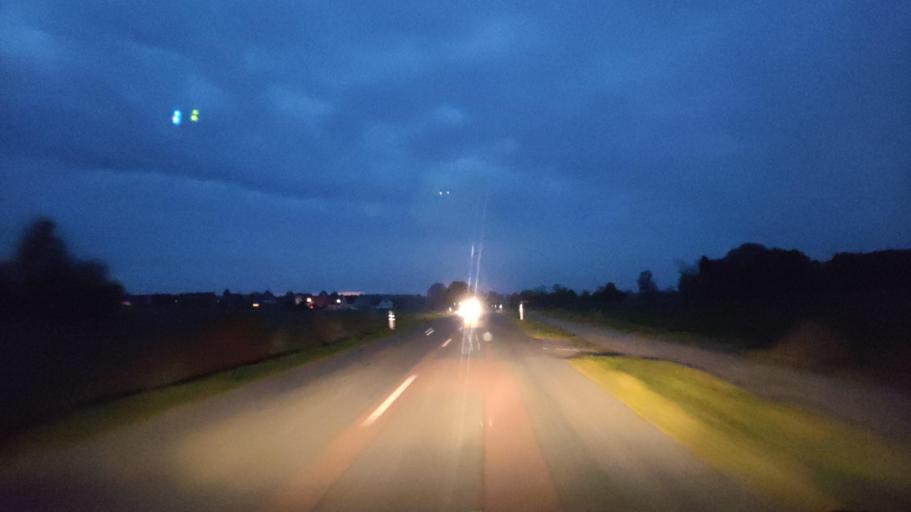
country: DE
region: Lower Saxony
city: Gross Twulpstedt
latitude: 52.3564
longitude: 10.9192
